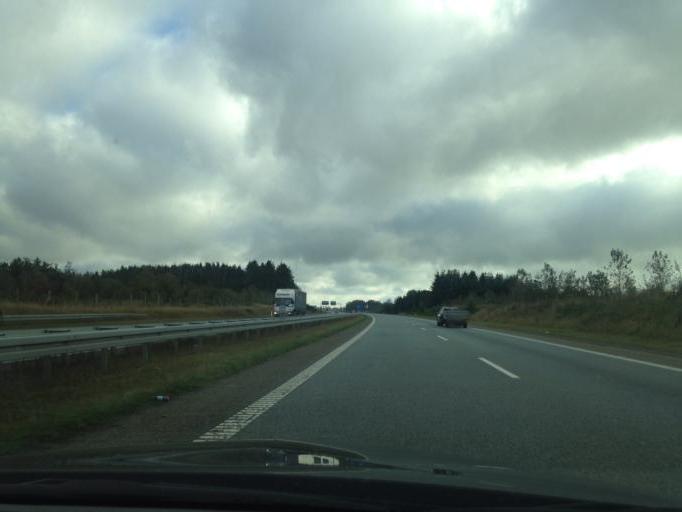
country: DK
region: South Denmark
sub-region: Vejle Kommune
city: Give
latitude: 55.8371
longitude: 9.2897
